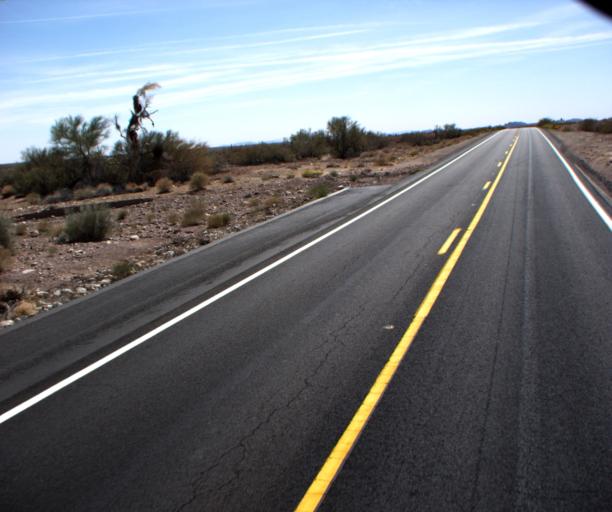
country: US
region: Arizona
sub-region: La Paz County
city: Quartzsite
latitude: 33.1944
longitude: -114.2715
